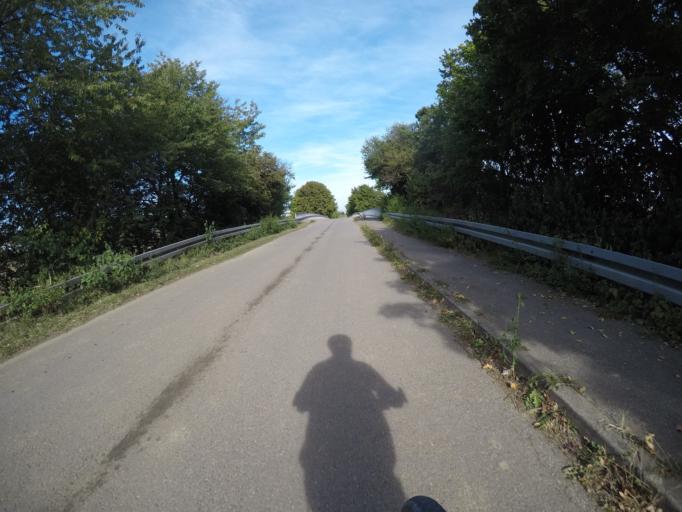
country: DE
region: Baden-Wuerttemberg
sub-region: Regierungsbezirk Stuttgart
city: Korntal
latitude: 48.8420
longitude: 9.1107
